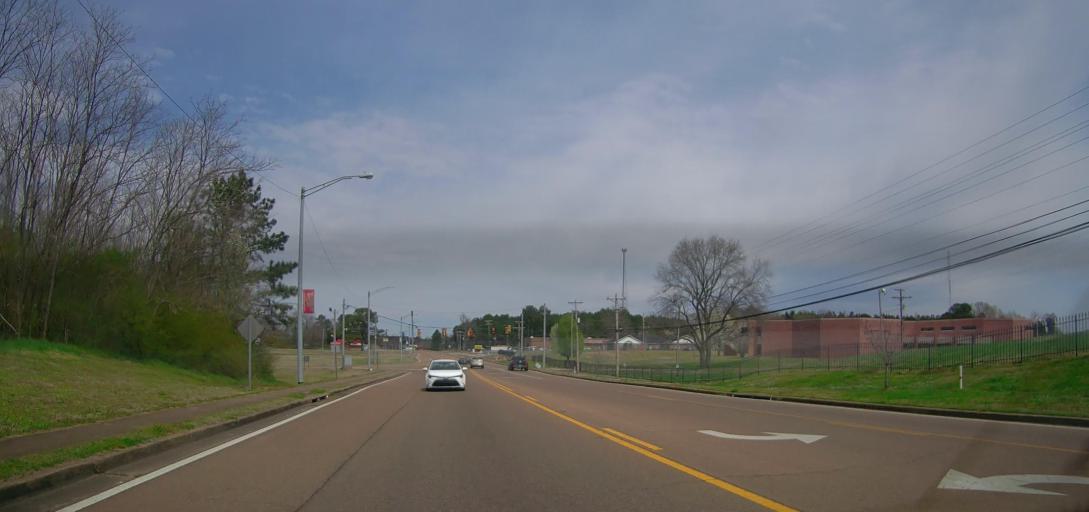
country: US
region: Mississippi
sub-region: Marshall County
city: Holly Springs
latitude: 34.7774
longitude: -89.4486
